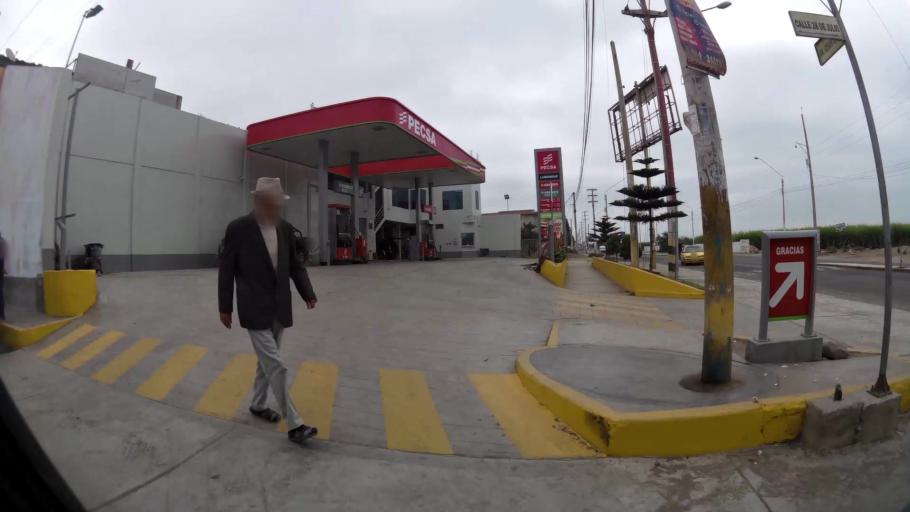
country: PE
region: La Libertad
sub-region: Provincia de Trujillo
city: La Esperanza
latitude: -8.1000
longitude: -79.0624
